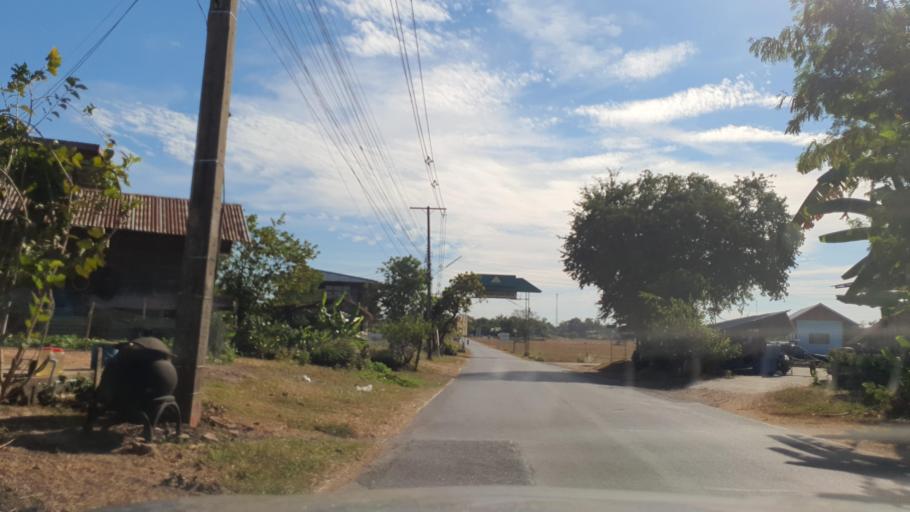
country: TH
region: Kalasin
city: Kuchinarai
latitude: 16.5539
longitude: 104.0979
